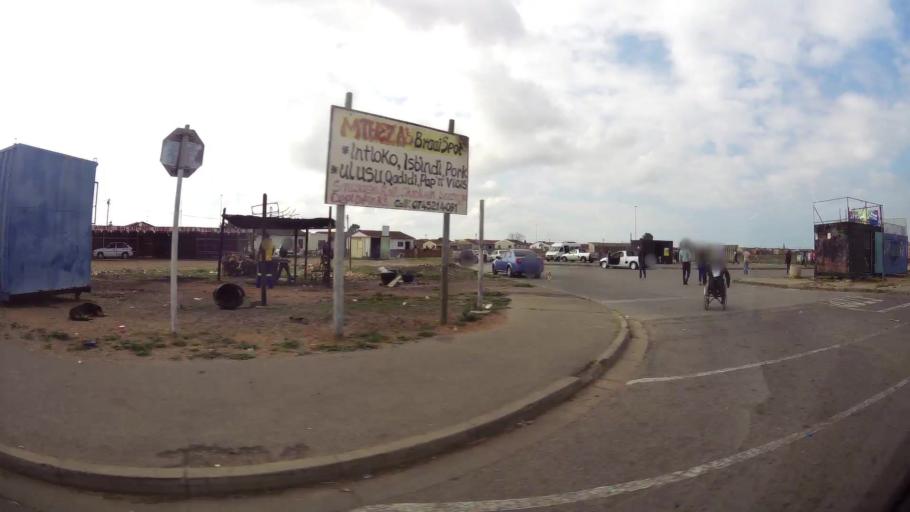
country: ZA
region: Eastern Cape
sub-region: Nelson Mandela Bay Metropolitan Municipality
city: Port Elizabeth
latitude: -33.8195
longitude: 25.5867
